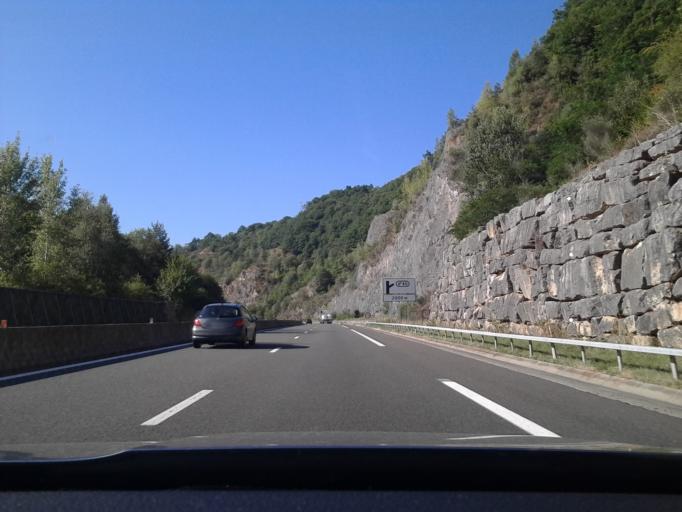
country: FR
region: Languedoc-Roussillon
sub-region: Departement de la Lozere
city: La Canourgue
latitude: 44.4565
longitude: 3.1914
